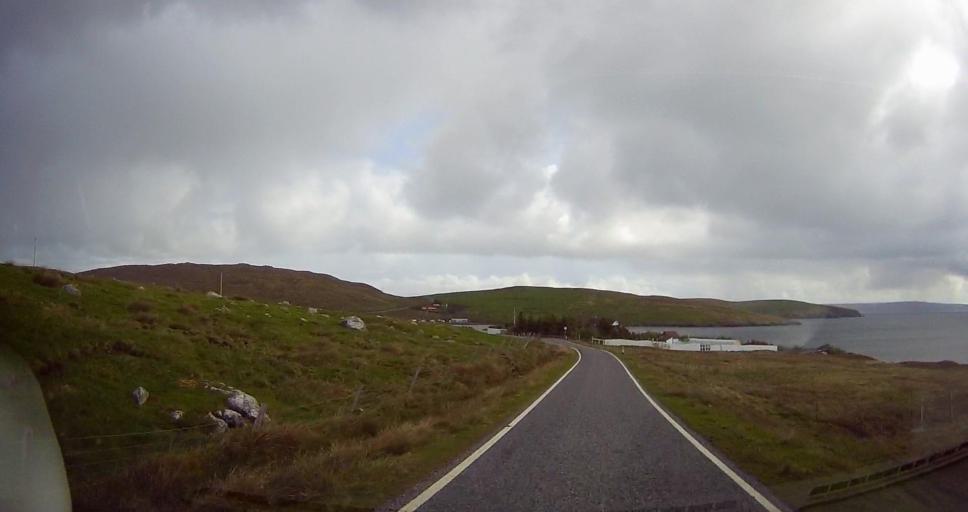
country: GB
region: Scotland
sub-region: Shetland Islands
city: Lerwick
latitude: 60.5348
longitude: -1.3595
